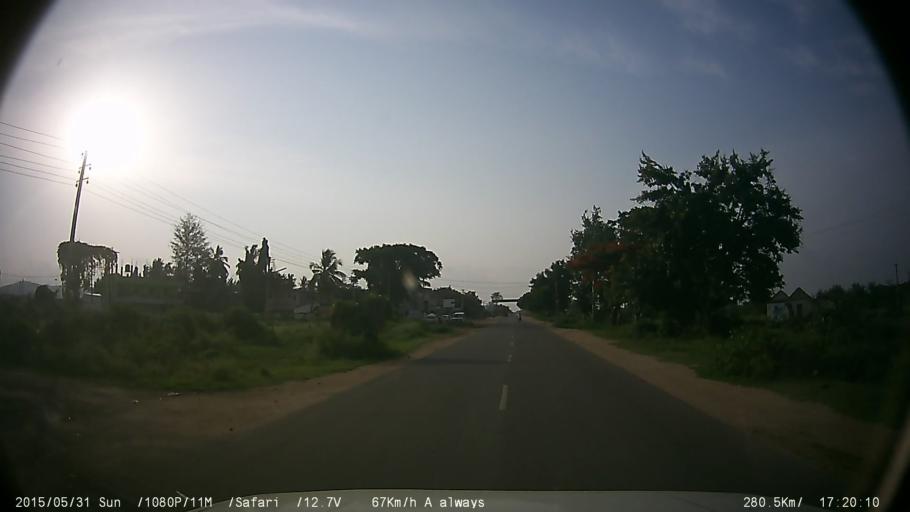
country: IN
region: Karnataka
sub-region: Chamrajnagar
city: Gundlupet
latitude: 11.8209
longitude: 76.6824
